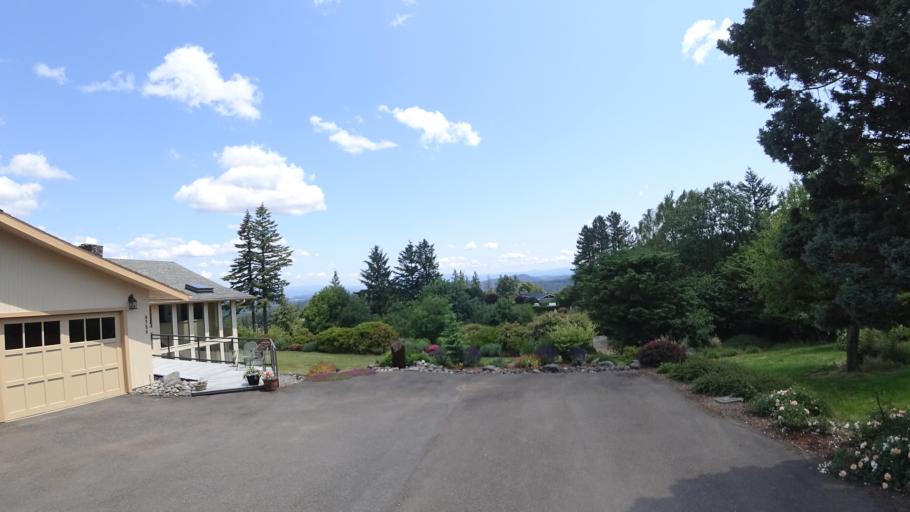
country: US
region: Oregon
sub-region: Clackamas County
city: Happy Valley
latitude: 45.4518
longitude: -122.5461
